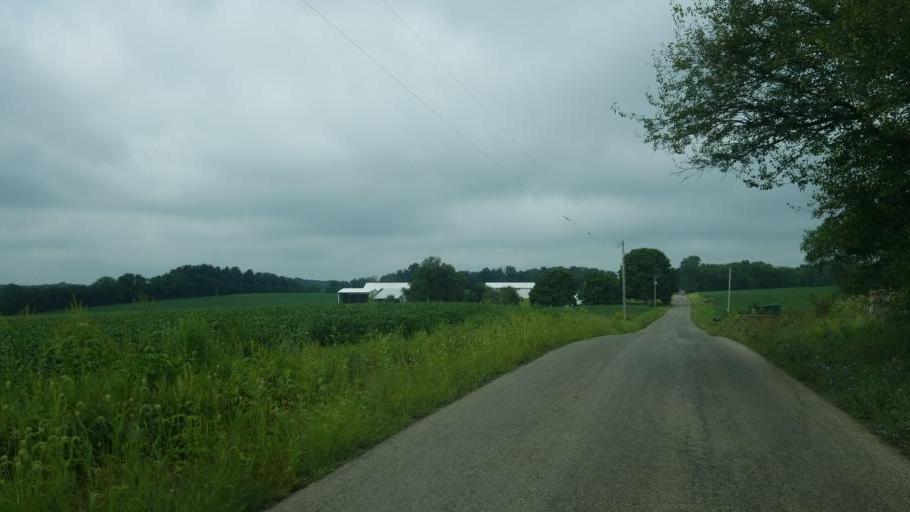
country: US
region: Ohio
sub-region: Licking County
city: Utica
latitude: 40.2482
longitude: -82.3611
